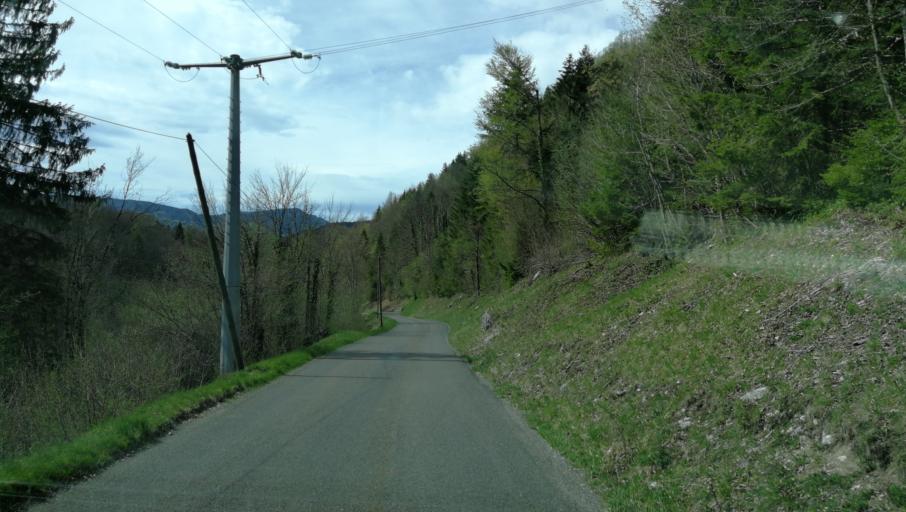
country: FR
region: Rhone-Alpes
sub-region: Departement de l'Ain
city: Chatillon-en-Michaille
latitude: 46.2064
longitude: 5.7498
